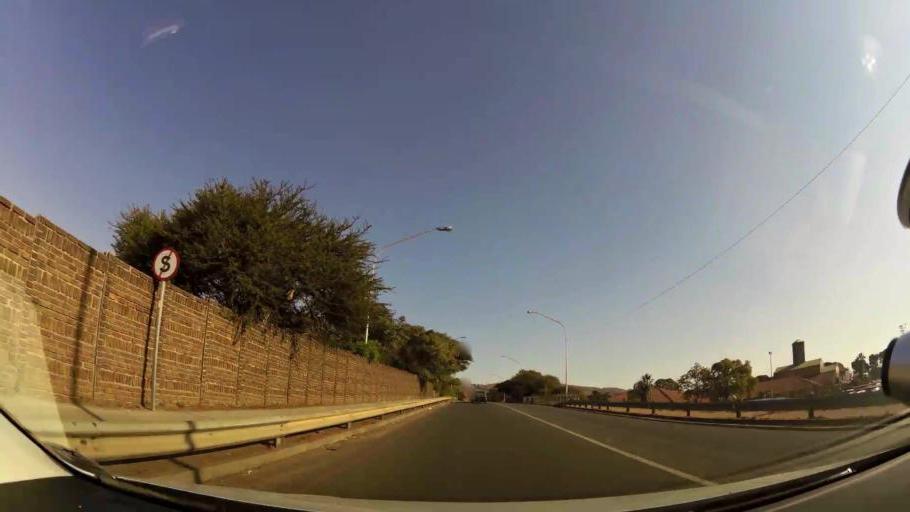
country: ZA
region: Gauteng
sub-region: City of Tshwane Metropolitan Municipality
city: Pretoria
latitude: -25.7169
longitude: 28.1546
